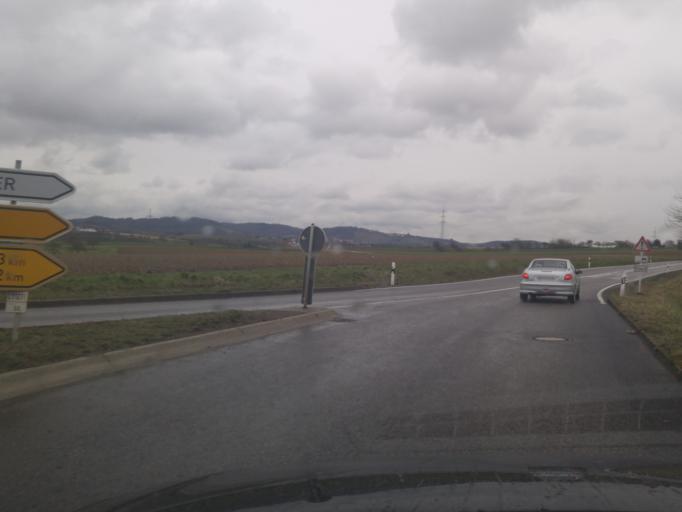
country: DE
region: Baden-Wuerttemberg
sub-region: Regierungsbezirk Stuttgart
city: Schwaikheim
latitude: 48.8925
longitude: 9.3639
